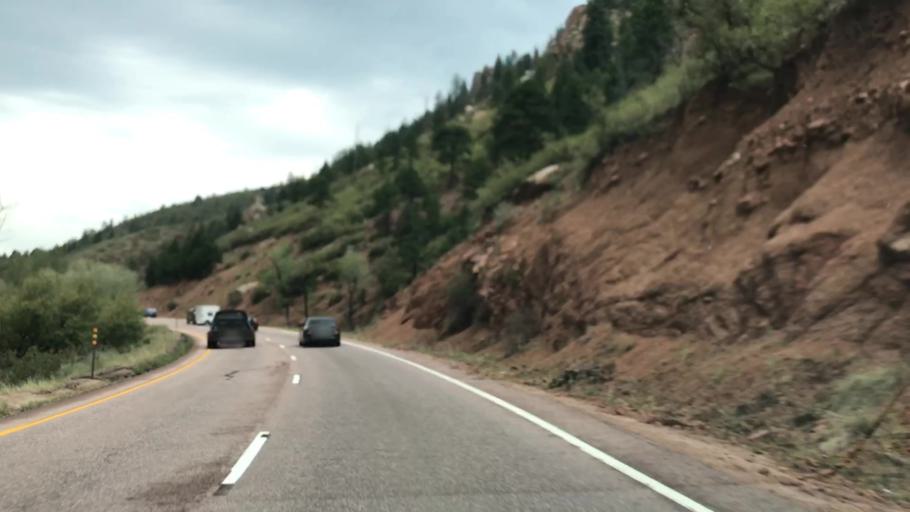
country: US
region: Colorado
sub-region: El Paso County
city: Manitou Springs
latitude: 38.8836
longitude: -104.9505
